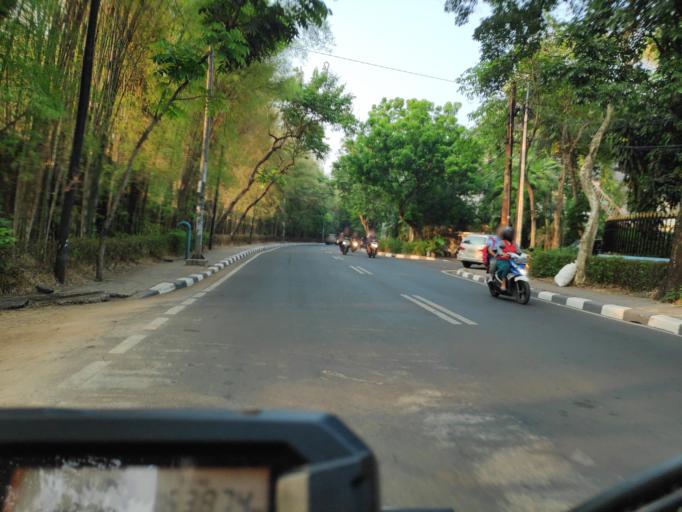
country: ID
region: Jakarta Raya
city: Jakarta
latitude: -6.2503
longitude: 106.8038
